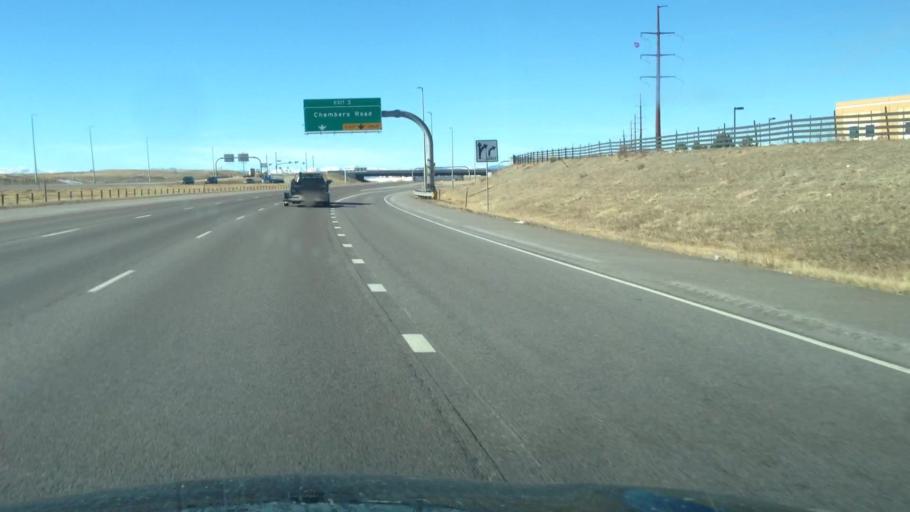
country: US
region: Colorado
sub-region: Douglas County
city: Stonegate
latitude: 39.5503
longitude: -104.8015
